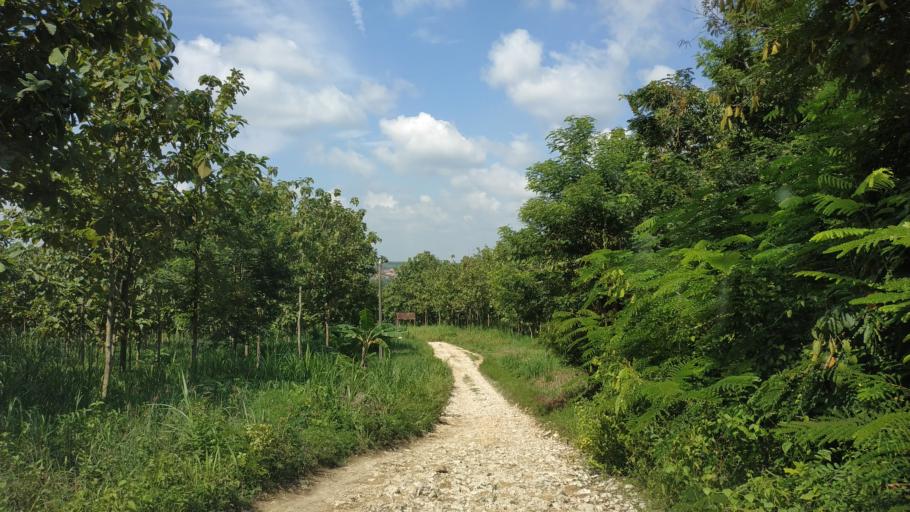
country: ID
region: Central Java
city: Guyangan
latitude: -7.0068
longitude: 111.0977
